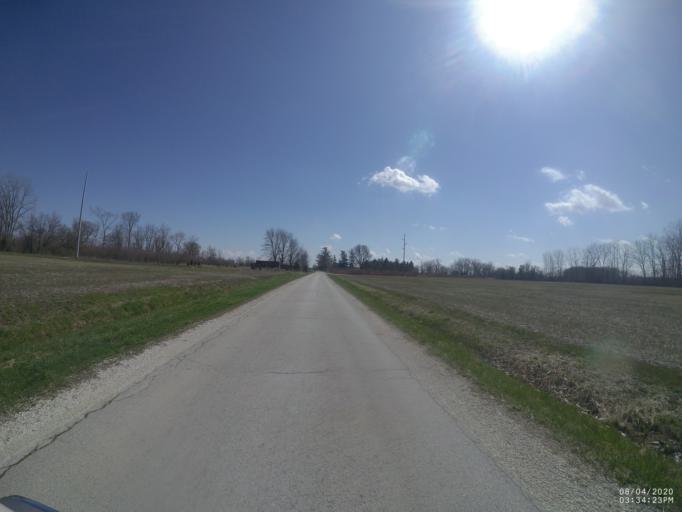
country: US
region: Ohio
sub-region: Sandusky County
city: Stony Prairie
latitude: 41.2637
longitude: -83.2574
